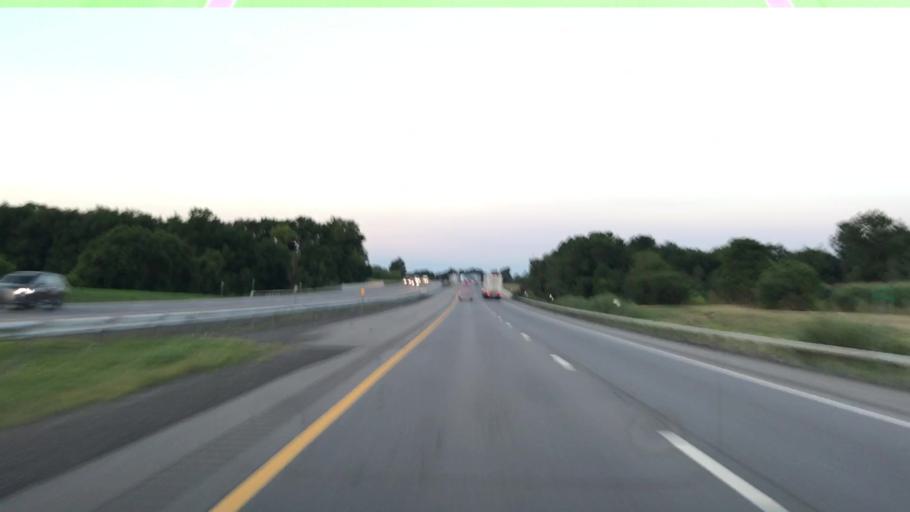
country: US
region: New York
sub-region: Chautauqua County
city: Silver Creek
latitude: 42.5166
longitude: -79.1550
